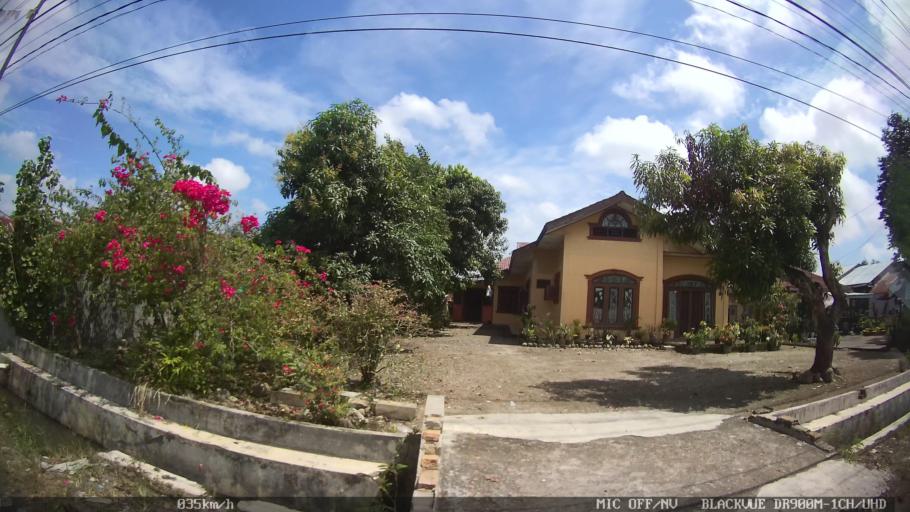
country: ID
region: North Sumatra
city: Percut
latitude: 3.6020
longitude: 98.7773
